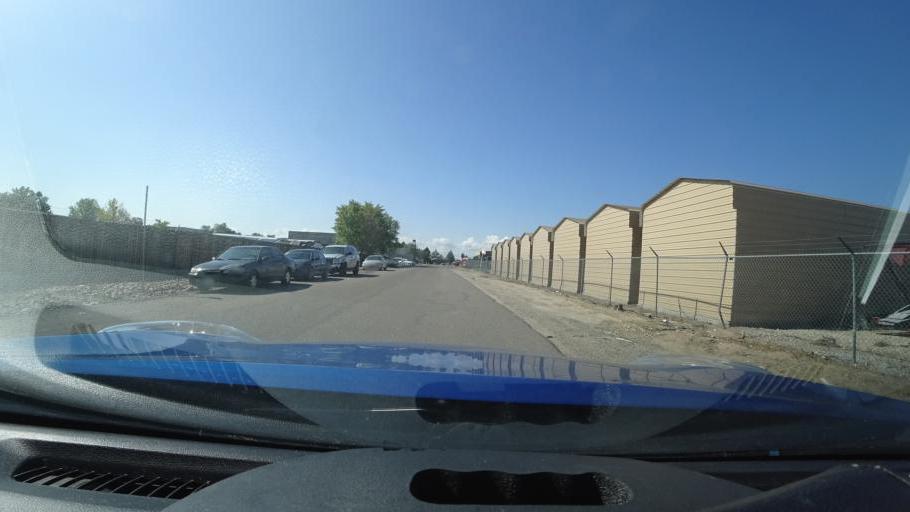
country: US
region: Colorado
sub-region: Adams County
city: Aurora
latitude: 39.7202
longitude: -104.7958
